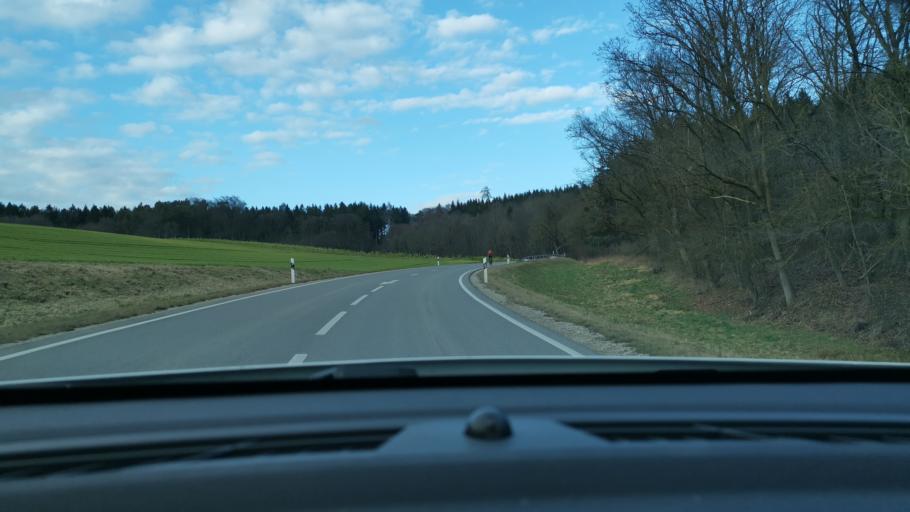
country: DE
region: Bavaria
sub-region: Swabia
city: Petersdorf
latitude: 48.5402
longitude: 11.0013
